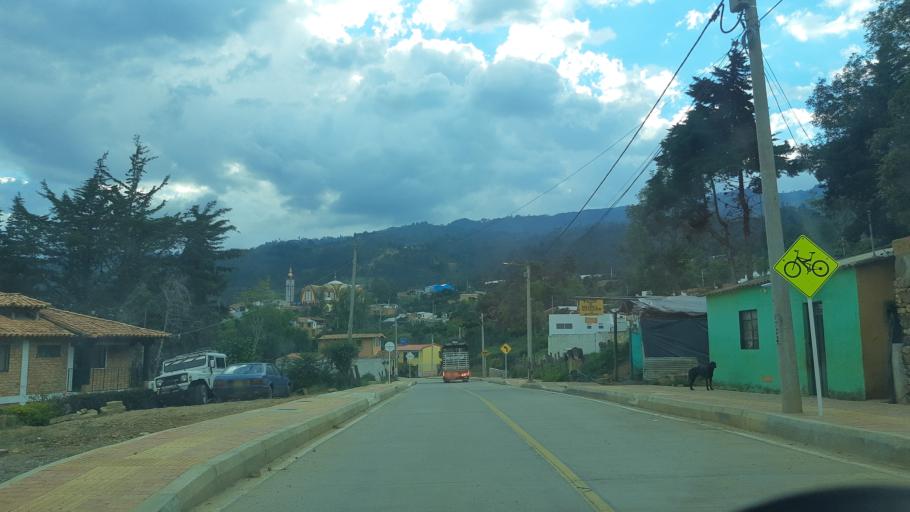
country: CO
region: Boyaca
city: Santa Sofia
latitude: 5.7159
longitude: -73.6005
